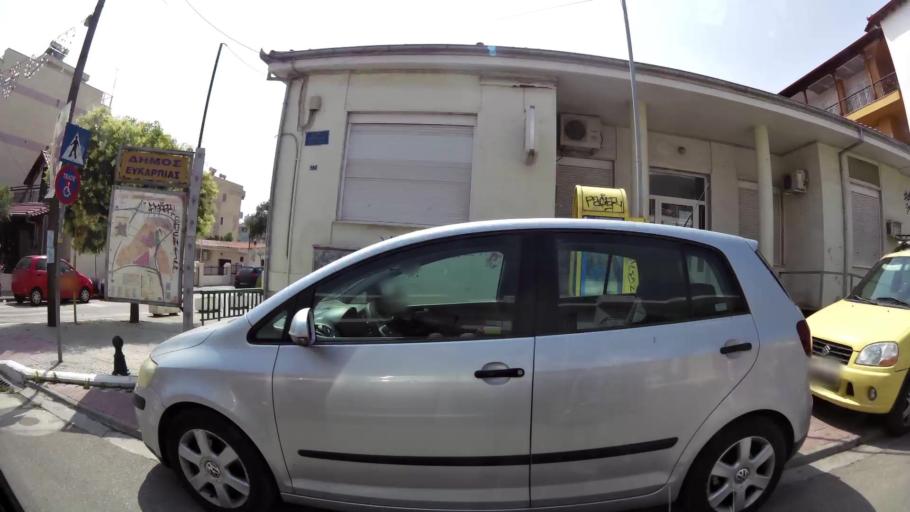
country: GR
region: Central Macedonia
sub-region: Nomos Thessalonikis
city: Efkarpia
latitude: 40.6872
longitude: 22.9539
